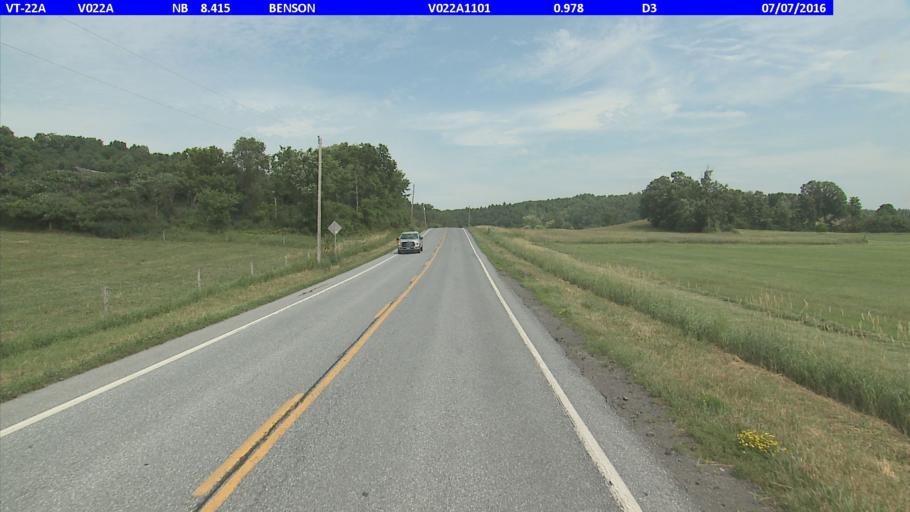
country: US
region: Vermont
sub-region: Rutland County
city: Fair Haven
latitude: 43.6833
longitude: -73.2895
